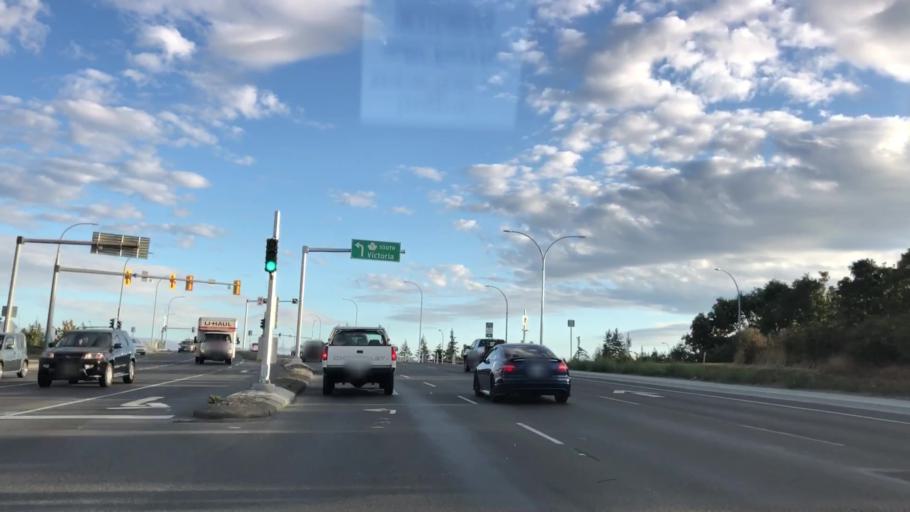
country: CA
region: British Columbia
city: Langford
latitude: 48.4585
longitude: -123.4976
